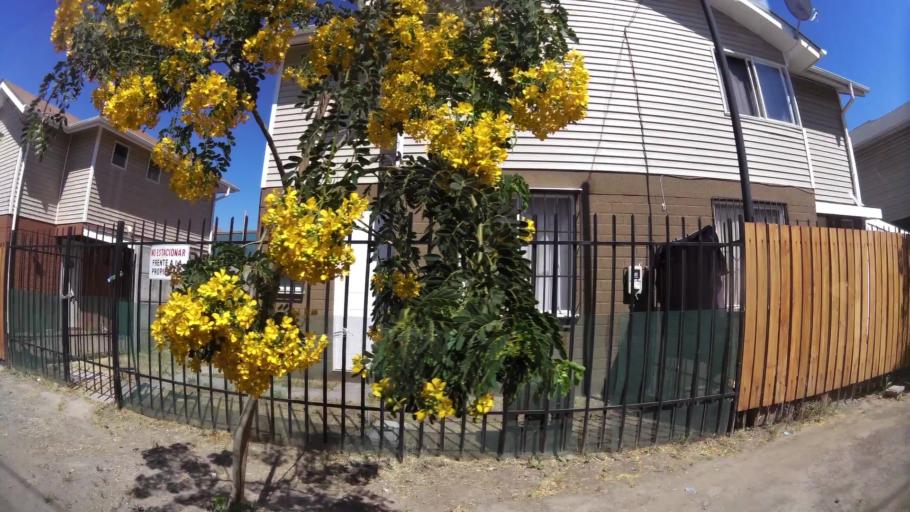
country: CL
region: Santiago Metropolitan
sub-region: Provincia de Maipo
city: San Bernardo
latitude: -33.6122
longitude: -70.6897
